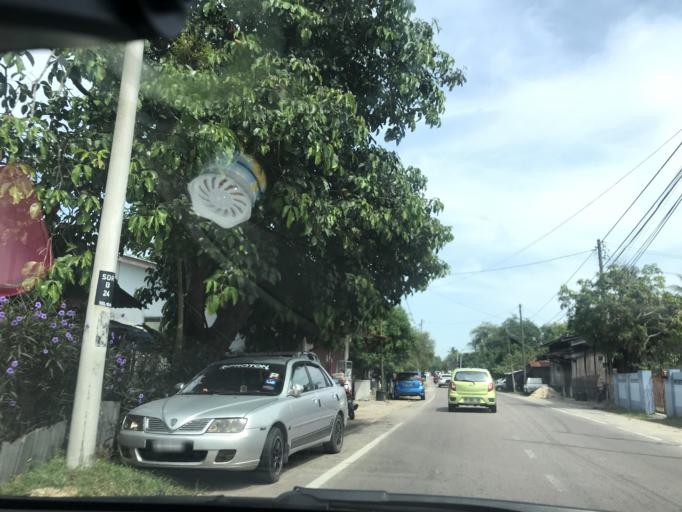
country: MY
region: Kelantan
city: Tumpat
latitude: 6.2008
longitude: 102.1602
